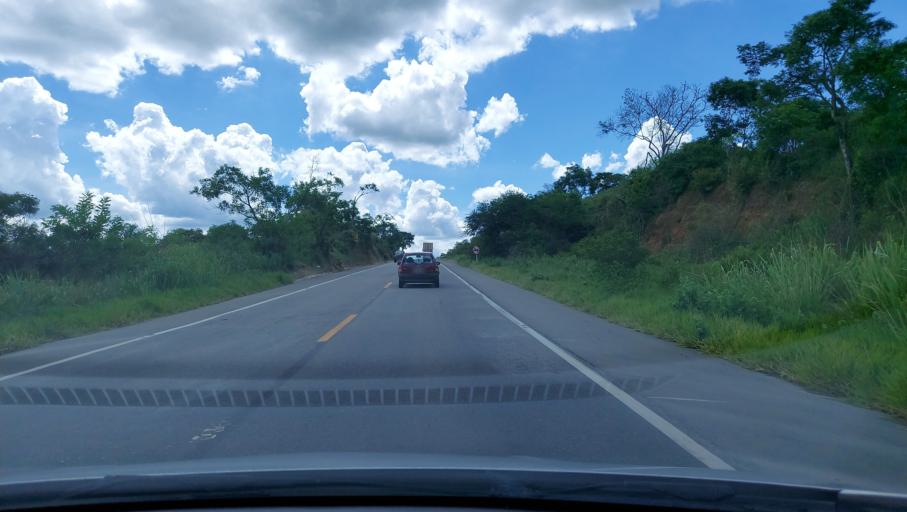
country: BR
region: Bahia
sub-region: Ruy Barbosa
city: Terra Nova
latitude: -12.4495
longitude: -40.6482
